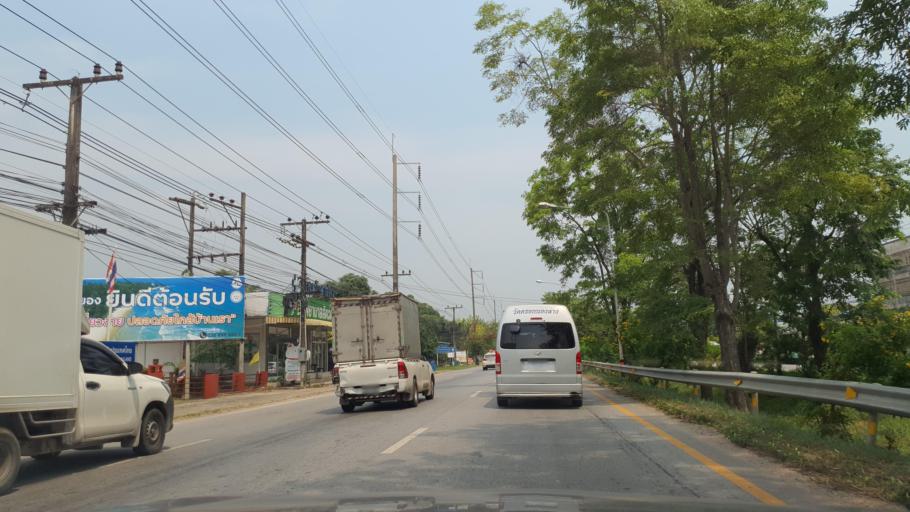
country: TH
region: Rayong
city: Rayong
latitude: 12.6455
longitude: 101.3535
